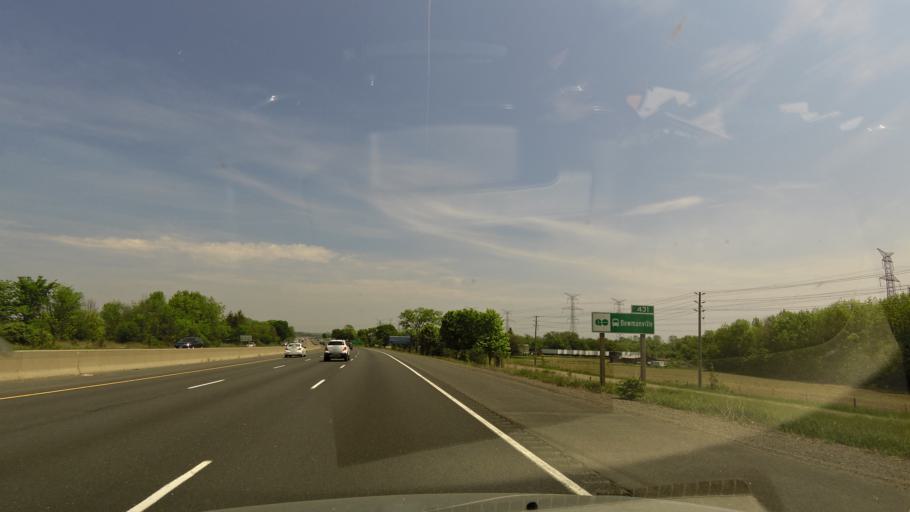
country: CA
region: Ontario
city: Oshawa
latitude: 43.8864
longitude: -78.7065
